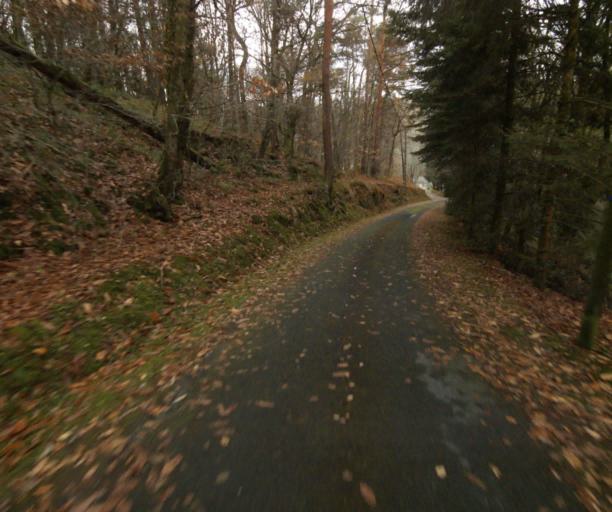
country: FR
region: Limousin
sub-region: Departement de la Correze
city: Chameyrat
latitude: 45.2294
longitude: 1.6918
